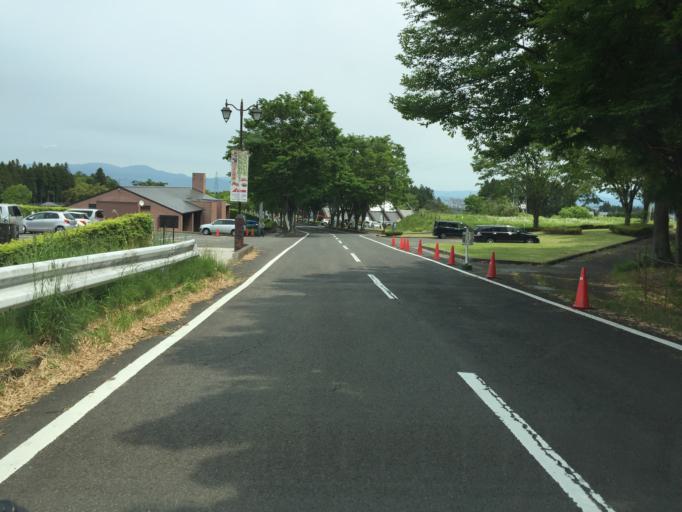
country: JP
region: Fukushima
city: Fukushima-shi
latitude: 37.7116
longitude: 140.3619
